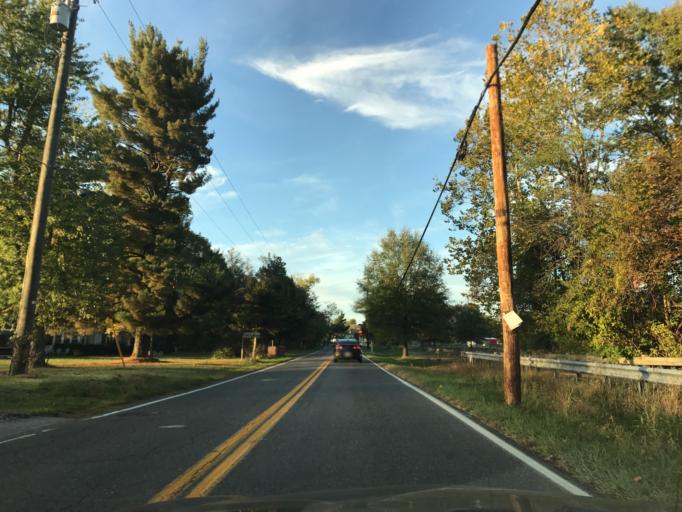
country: US
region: Maryland
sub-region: Anne Arundel County
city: Maryland City
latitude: 39.0859
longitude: -76.8230
